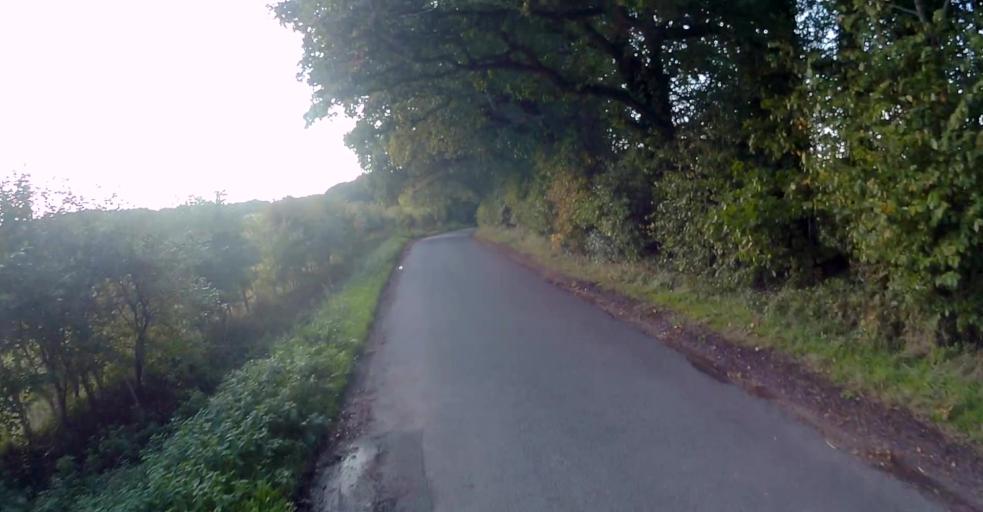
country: GB
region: England
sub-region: Hampshire
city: Long Sutton
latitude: 51.2096
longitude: -0.9015
